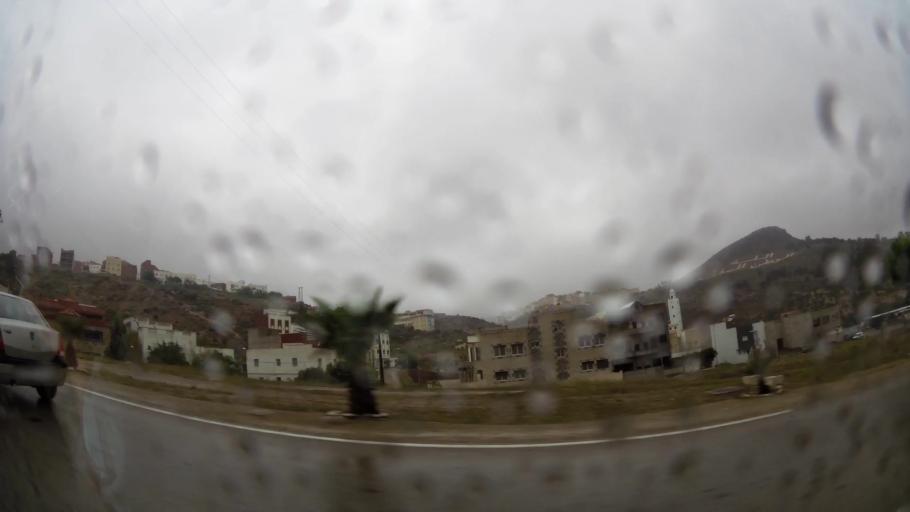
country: MA
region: Taza-Al Hoceima-Taounate
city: Al Hoceima
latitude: 35.2319
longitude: -3.9303
